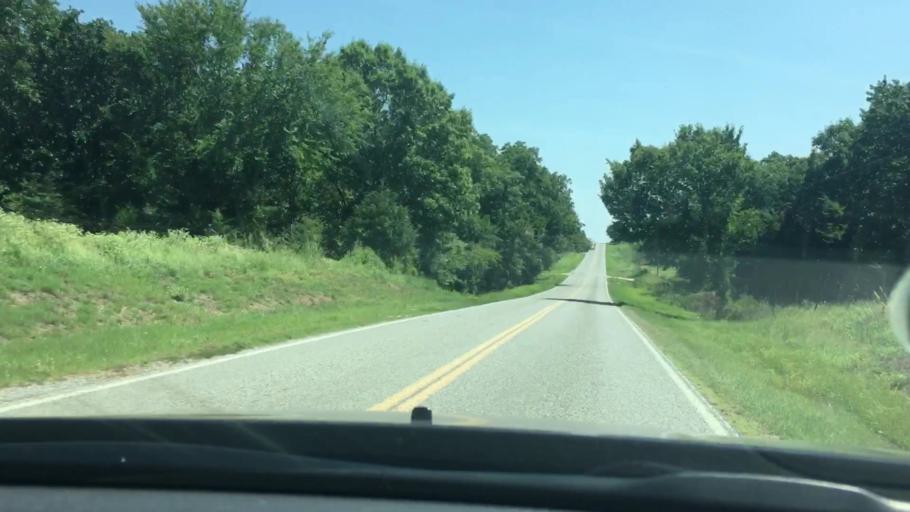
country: US
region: Oklahoma
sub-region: Johnston County
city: Tishomingo
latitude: 34.2741
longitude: -96.5332
